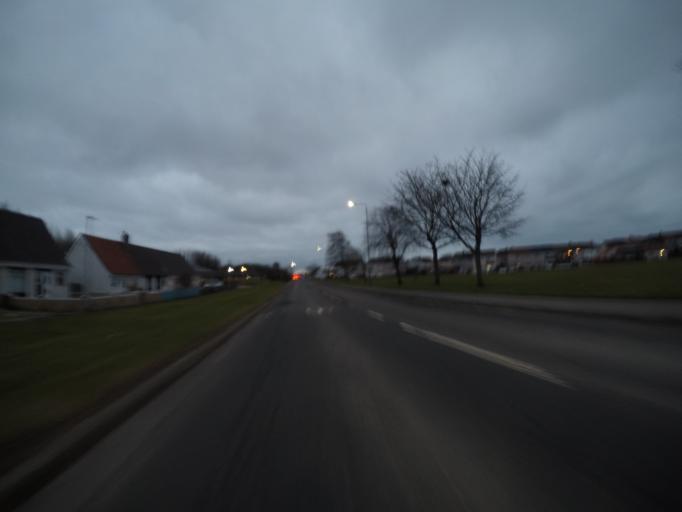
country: GB
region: Scotland
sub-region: North Ayrshire
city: Kilwinning
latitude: 55.6500
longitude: -4.6988
